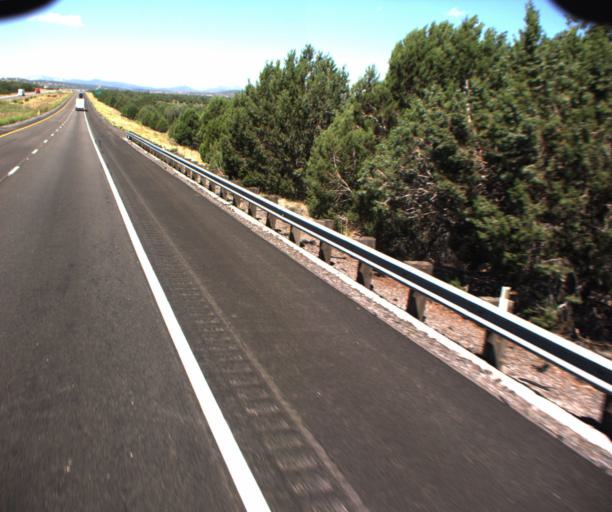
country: US
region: Arizona
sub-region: Mohave County
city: Peach Springs
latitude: 35.1913
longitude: -113.3367
